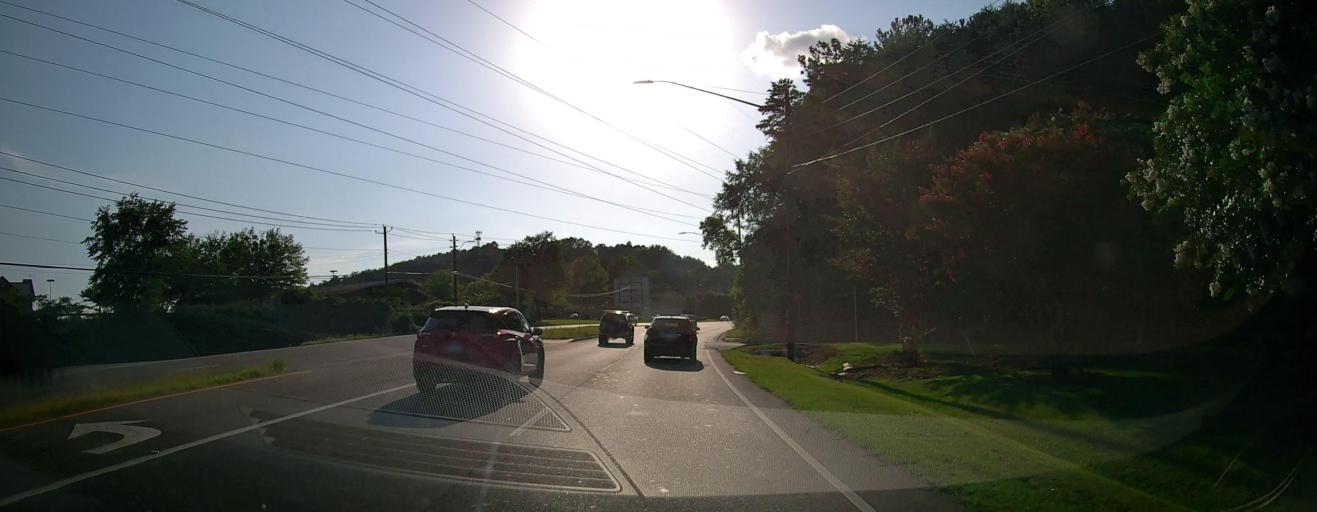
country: US
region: Alabama
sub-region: Jefferson County
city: Irondale
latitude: 33.5301
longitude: -86.7274
